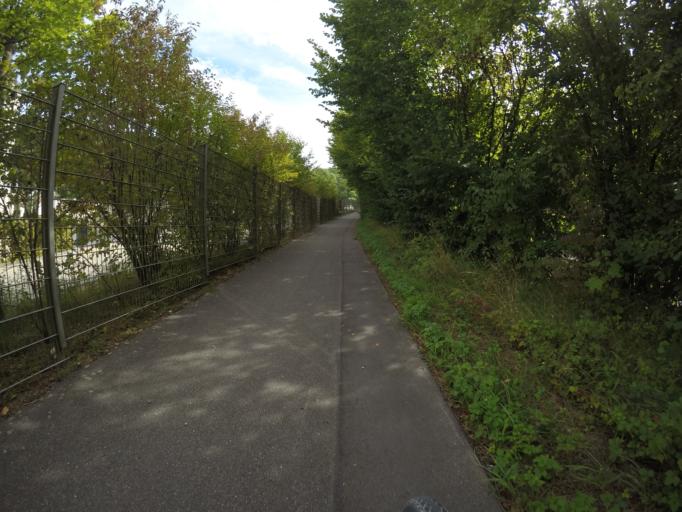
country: DE
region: Baden-Wuerttemberg
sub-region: Regierungsbezirk Stuttgart
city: Eberdingen
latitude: 48.9114
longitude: 8.9802
